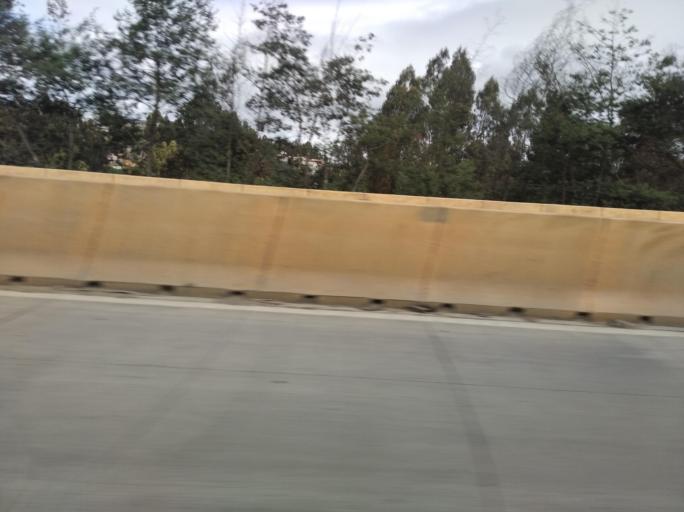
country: CL
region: Valparaiso
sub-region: Provincia de Valparaiso
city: Vina del Mar
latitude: -33.1067
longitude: -71.5635
